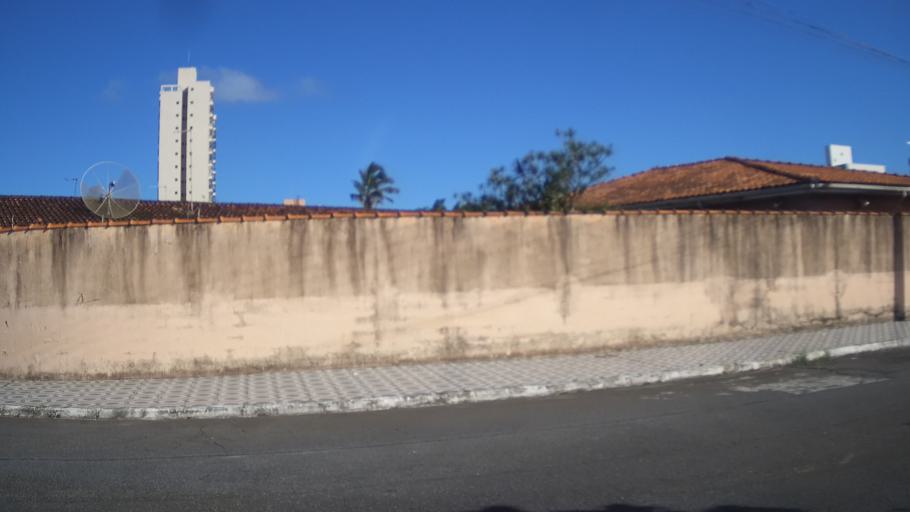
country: BR
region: Sao Paulo
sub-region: Mongagua
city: Mongagua
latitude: -24.0597
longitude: -46.5496
